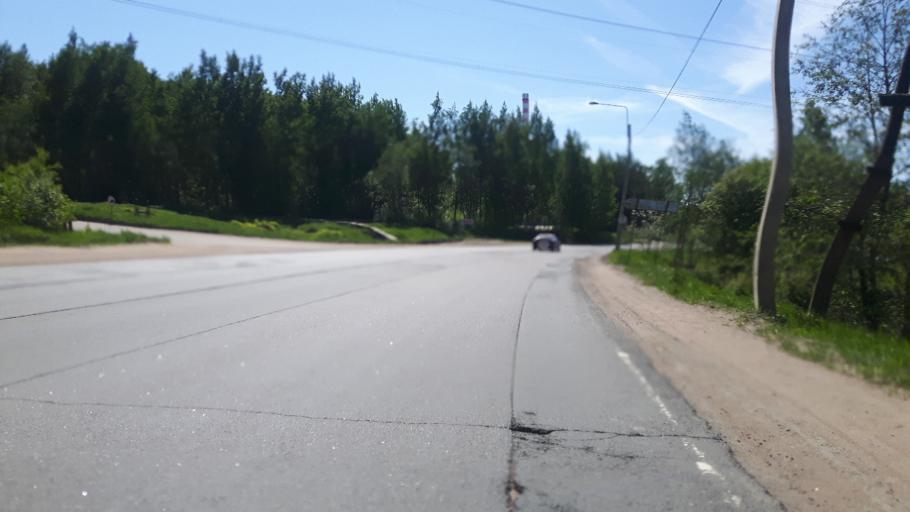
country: RU
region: Leningrad
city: Sosnovyy Bor
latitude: 59.8568
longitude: 29.0599
